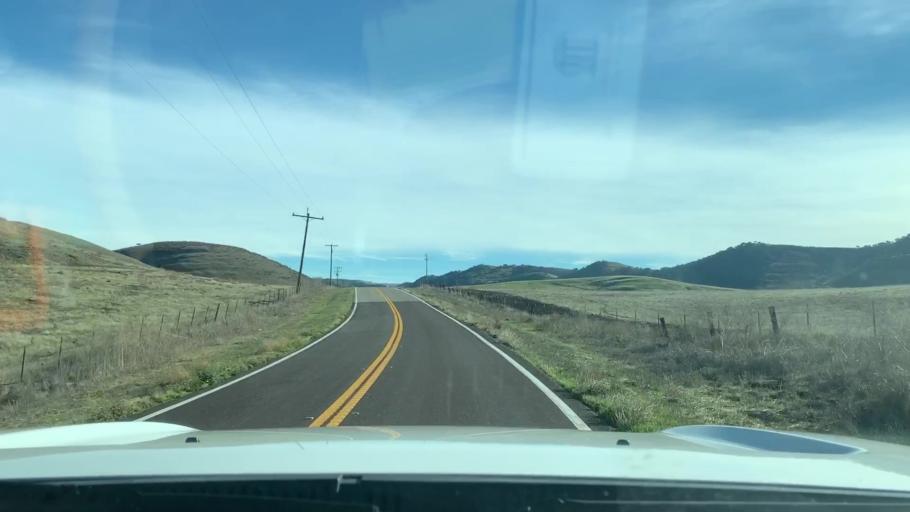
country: US
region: California
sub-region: Monterey County
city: King City
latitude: 36.1650
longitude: -120.8654
